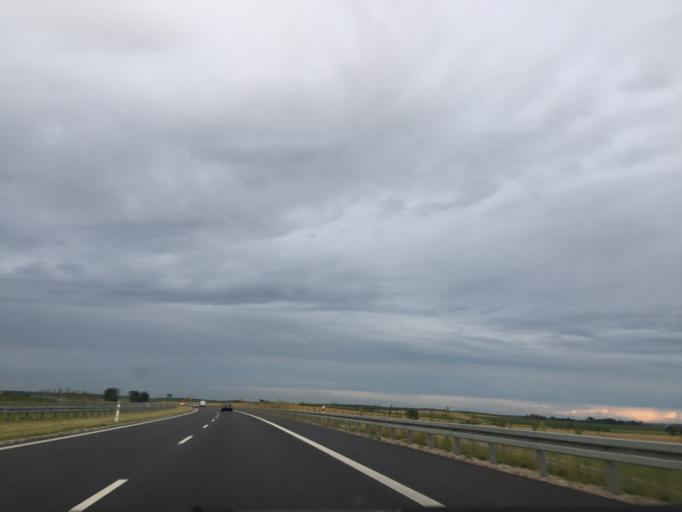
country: PL
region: Podlasie
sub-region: Powiat zambrowski
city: Rutki-Kossaki
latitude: 53.0852
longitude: 22.4796
